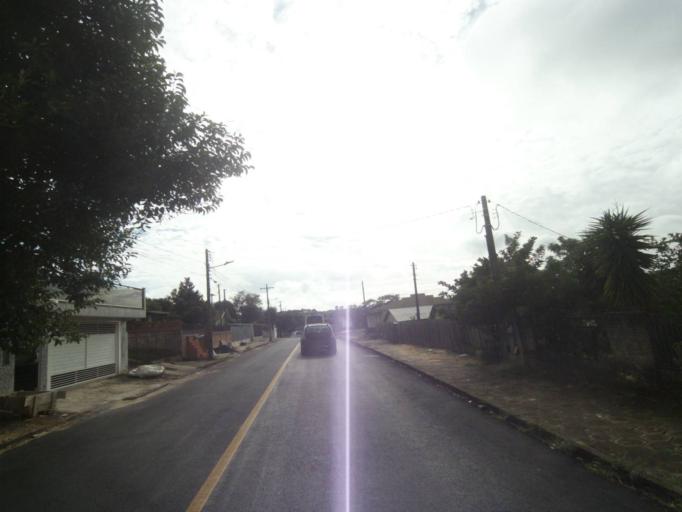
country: BR
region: Parana
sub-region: Telemaco Borba
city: Telemaco Borba
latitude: -24.3341
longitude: -50.6188
